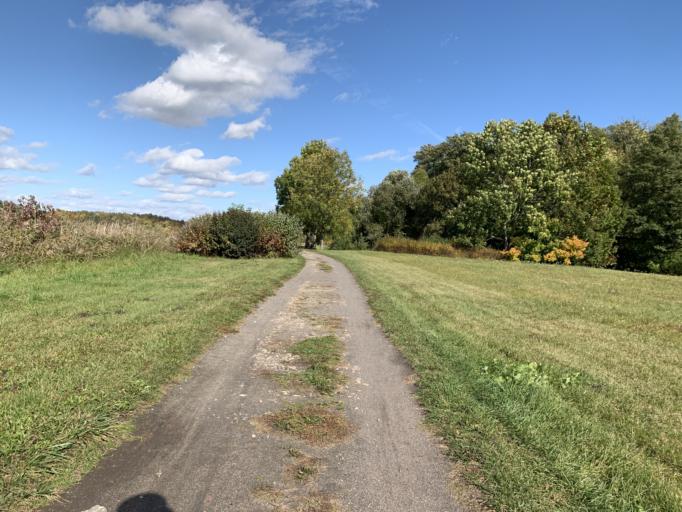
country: BY
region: Minsk
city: Nyasvizh
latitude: 53.2253
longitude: 26.7008
